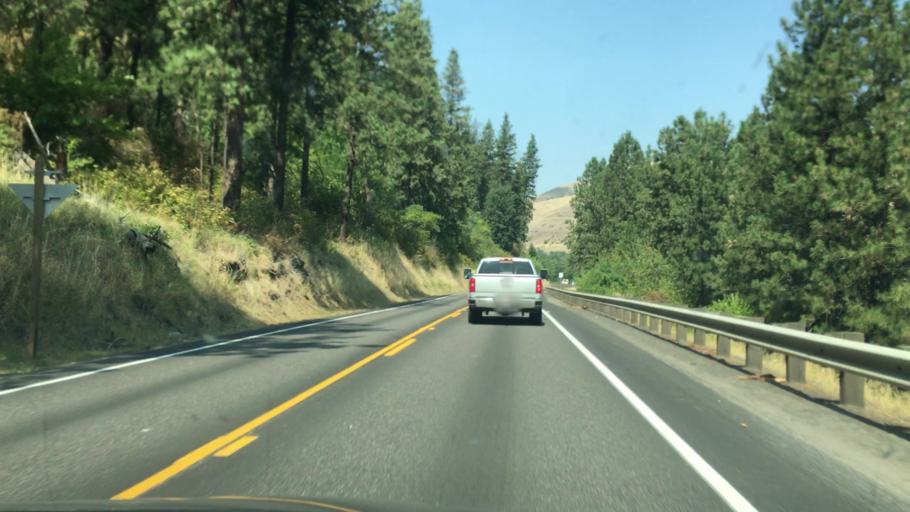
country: US
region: Idaho
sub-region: Clearwater County
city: Orofino
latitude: 46.4960
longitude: -116.4646
